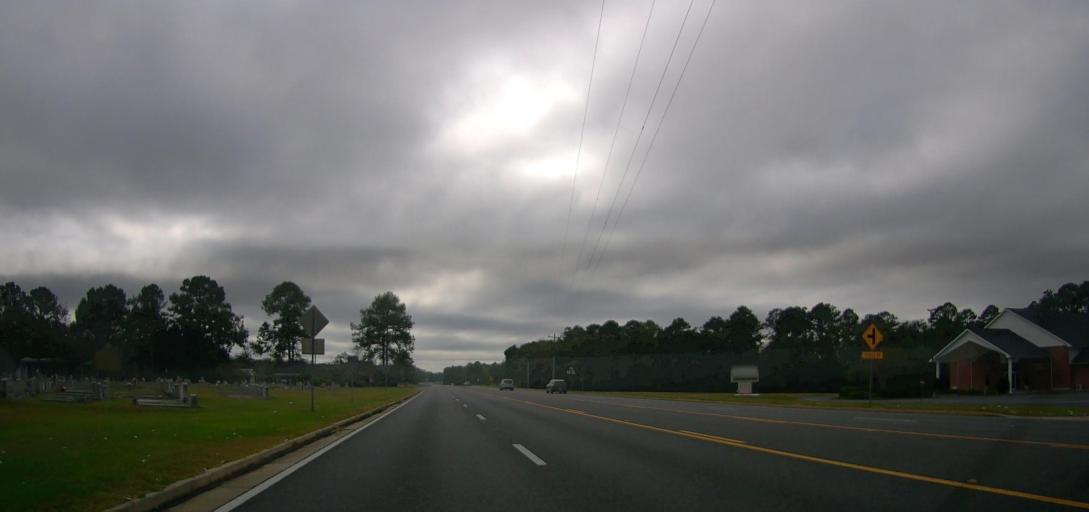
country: US
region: Georgia
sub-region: Colquitt County
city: Moultrie
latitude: 31.0707
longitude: -83.8238
